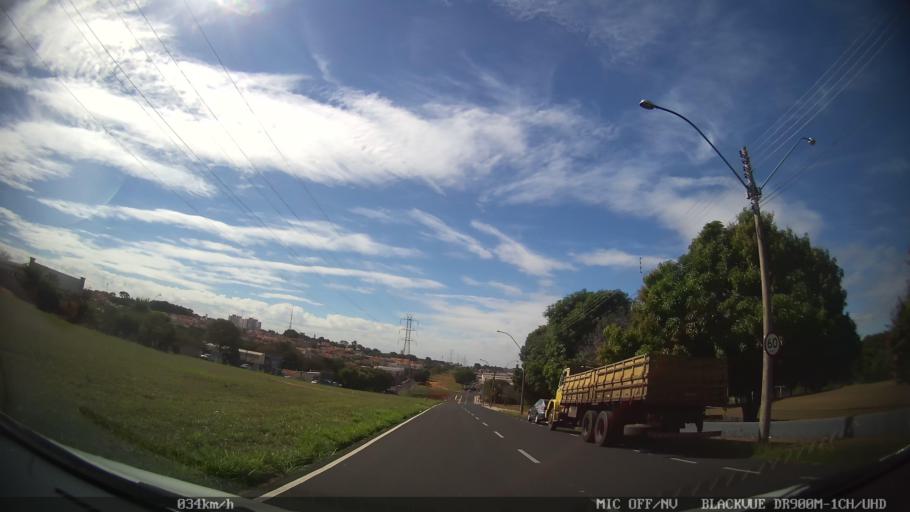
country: BR
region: Sao Paulo
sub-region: Sao Jose Do Rio Preto
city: Sao Jose do Rio Preto
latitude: -20.8437
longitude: -49.3630
